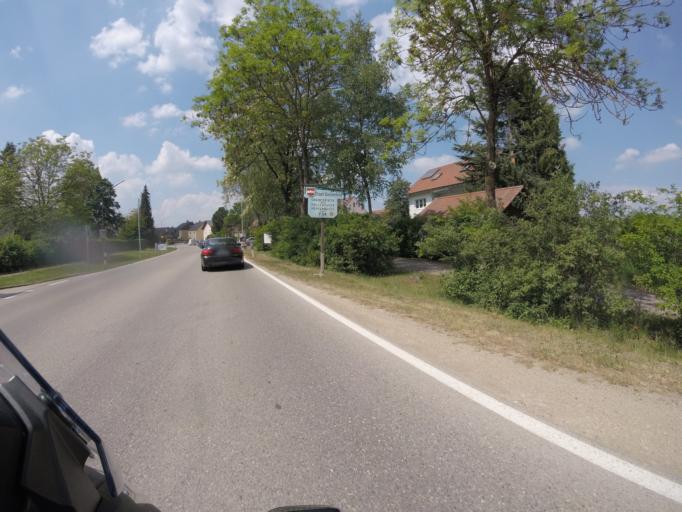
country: DE
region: Bavaria
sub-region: Upper Bavaria
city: Geisenfeld
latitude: 48.6873
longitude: 11.6227
